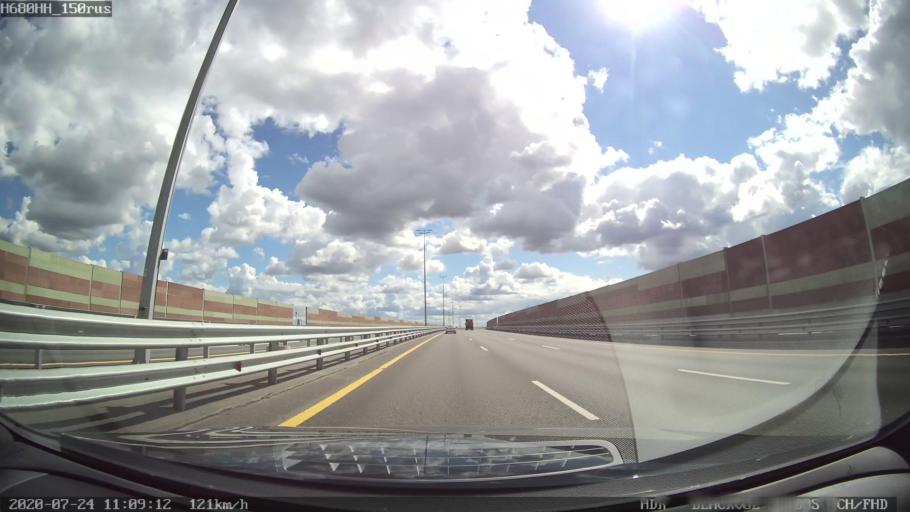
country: RU
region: St.-Petersburg
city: Tyarlevo
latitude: 59.7504
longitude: 30.4667
